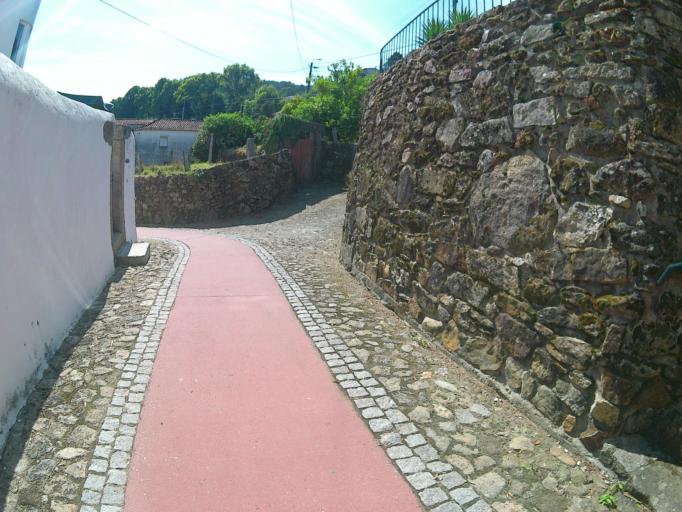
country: ES
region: Galicia
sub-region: Provincia de Pontevedra
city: O Rosal
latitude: 41.9015
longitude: -8.8107
